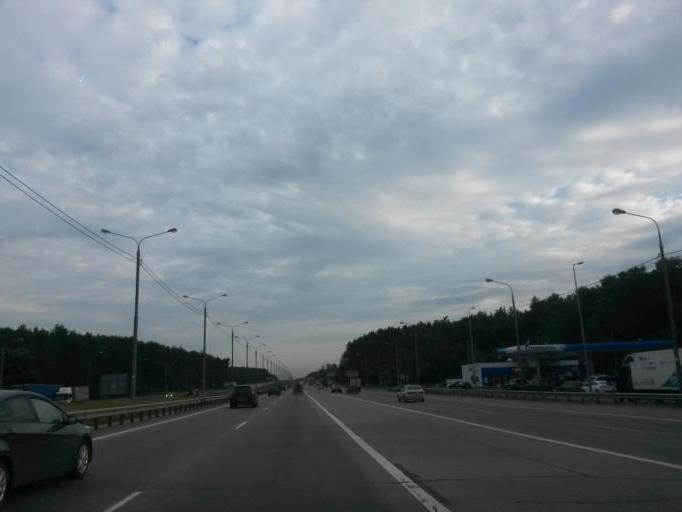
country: RU
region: Moskovskaya
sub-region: Podol'skiy Rayon
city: Podol'sk
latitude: 55.4256
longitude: 37.6124
